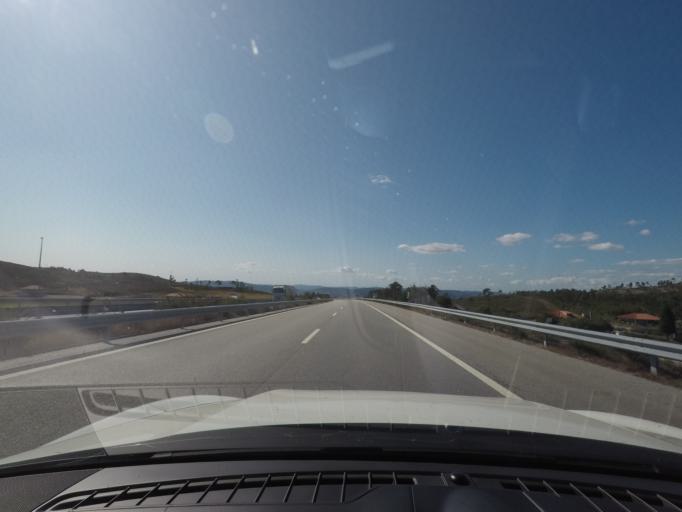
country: PT
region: Braga
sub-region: Fafe
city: Fafe
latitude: 41.4442
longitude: -8.0899
